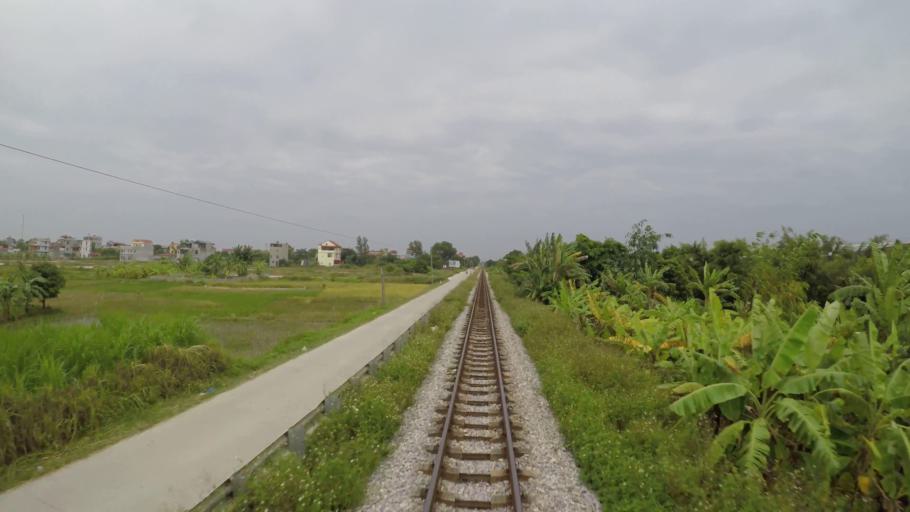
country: VN
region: Hai Duong
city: Lai Cach
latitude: 20.9520
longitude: 106.2332
